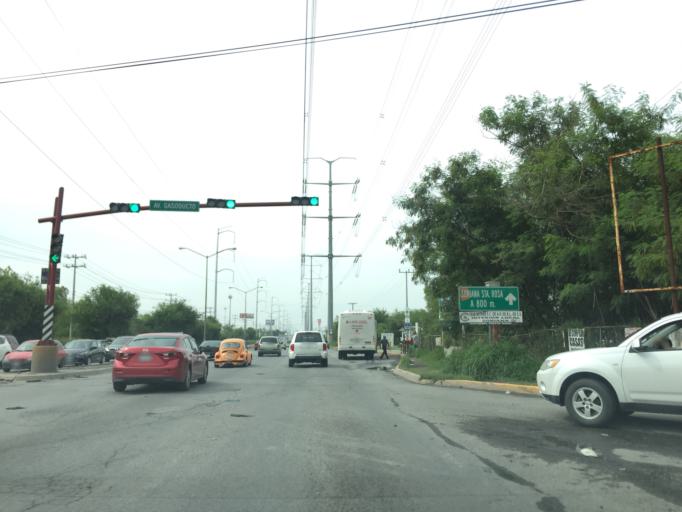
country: MX
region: Nuevo Leon
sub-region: Apodaca
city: Fraccionamiento Cosmopolis Octavo Sector
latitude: 25.7961
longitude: -100.2236
